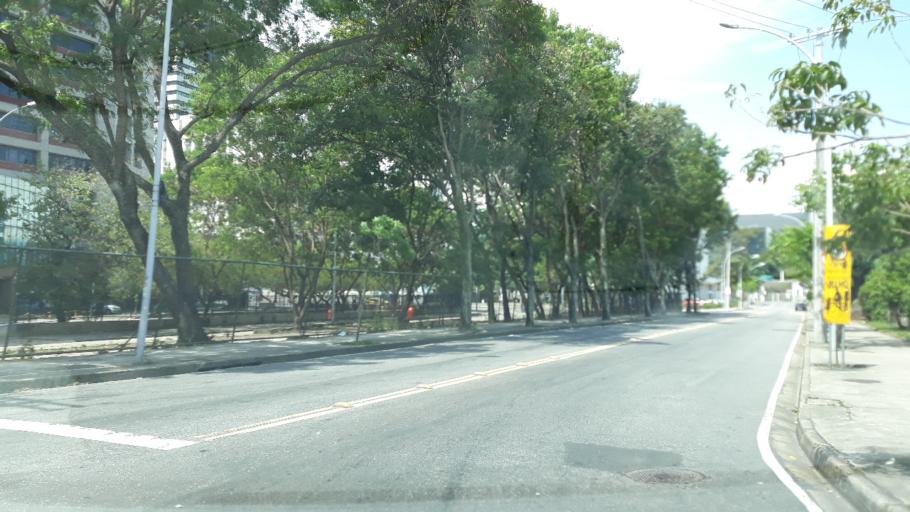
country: BR
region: Rio de Janeiro
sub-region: Rio De Janeiro
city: Rio de Janeiro
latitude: -22.9125
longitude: -43.2050
